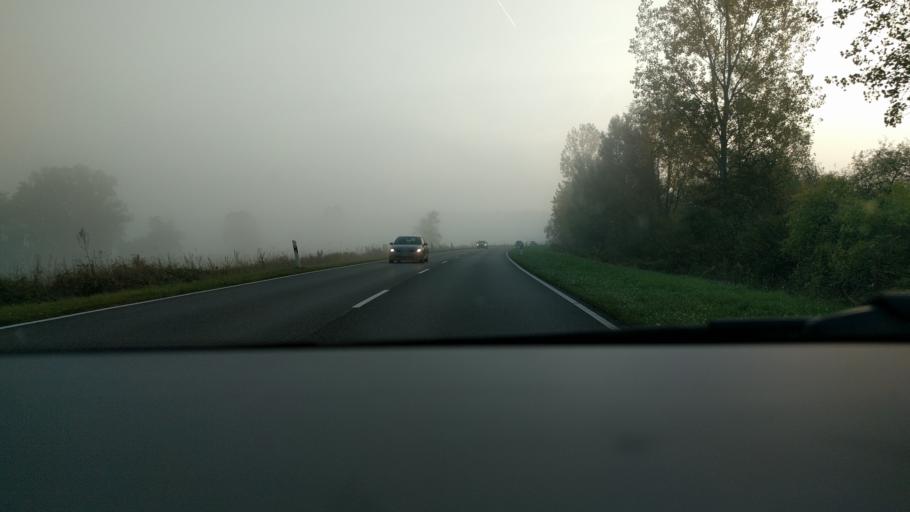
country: DE
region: Lower Saxony
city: Osloss
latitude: 52.4375
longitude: 10.6763
